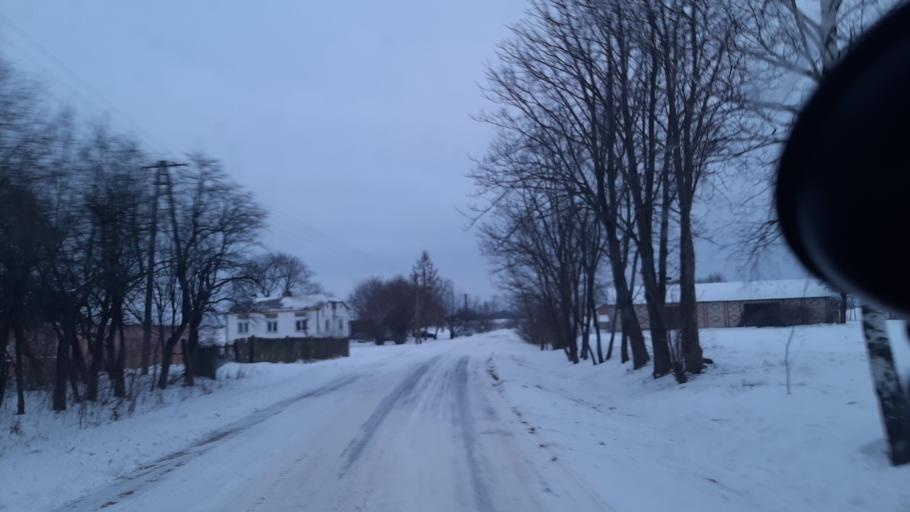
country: PL
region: Lublin Voivodeship
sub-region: Powiat lubelski
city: Jastkow
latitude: 51.3453
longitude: 22.4100
